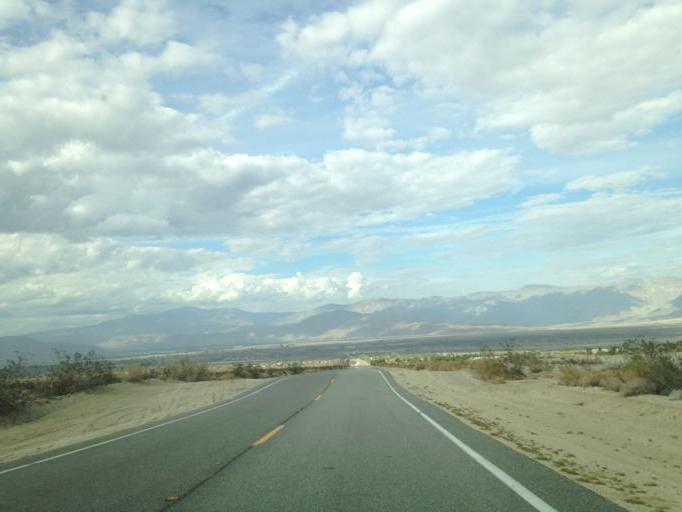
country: US
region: California
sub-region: San Diego County
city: Borrego Springs
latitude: 33.1874
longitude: -116.3307
